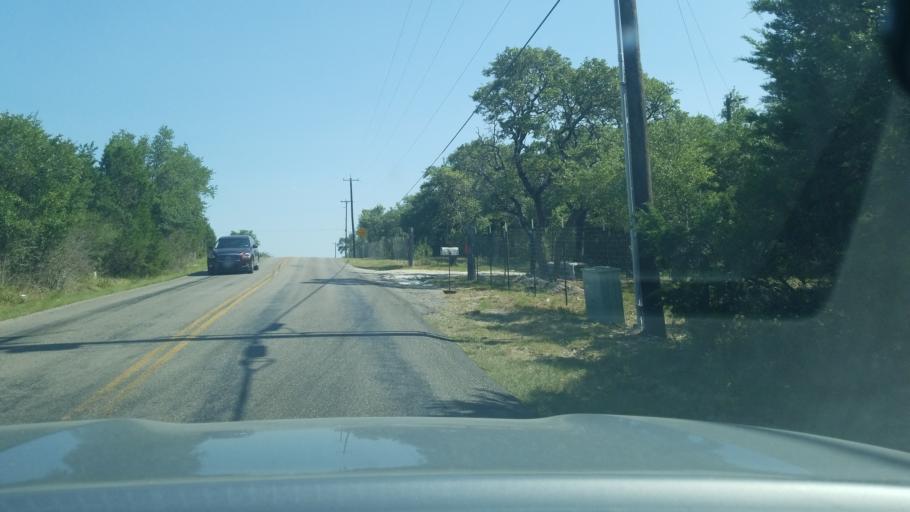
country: US
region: Texas
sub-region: Comal County
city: Bulverde
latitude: 29.7575
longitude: -98.5128
